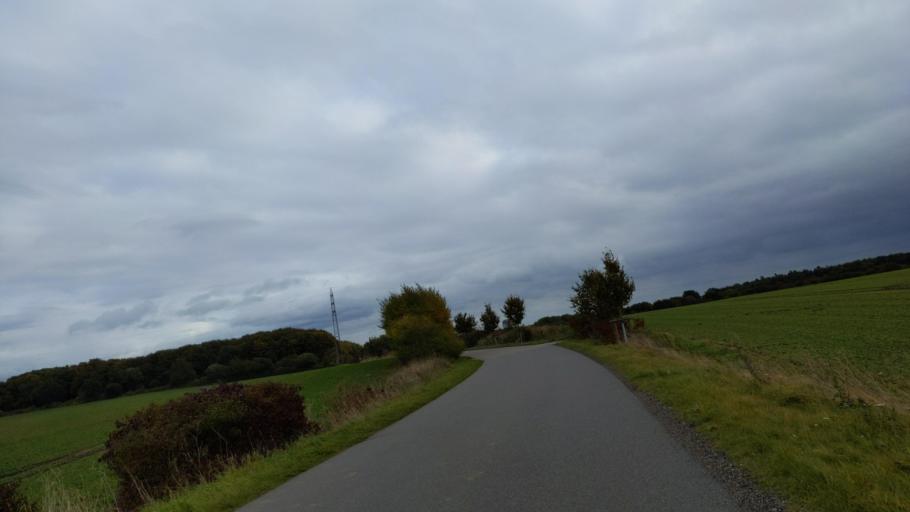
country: DE
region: Schleswig-Holstein
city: Sierksdorf
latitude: 54.0690
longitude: 10.7457
